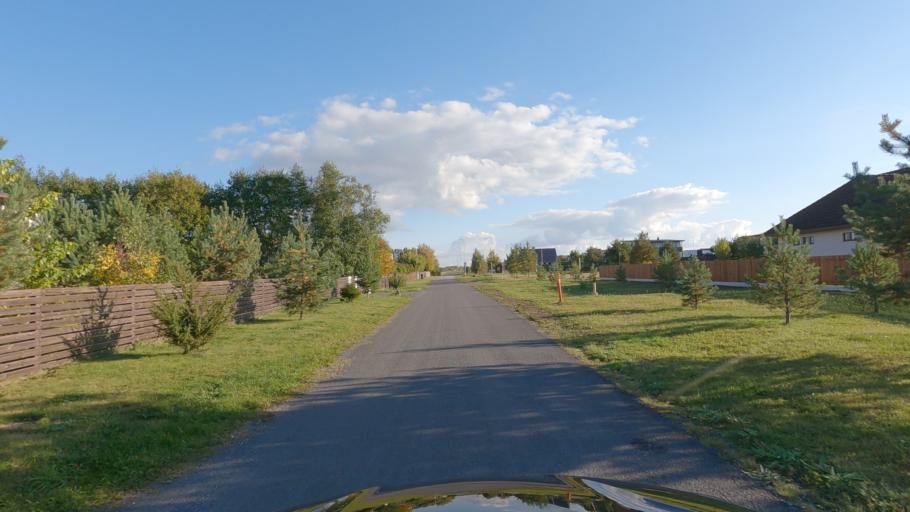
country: EE
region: Harju
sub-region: Saue vald
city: Laagri
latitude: 59.3451
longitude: 24.6499
